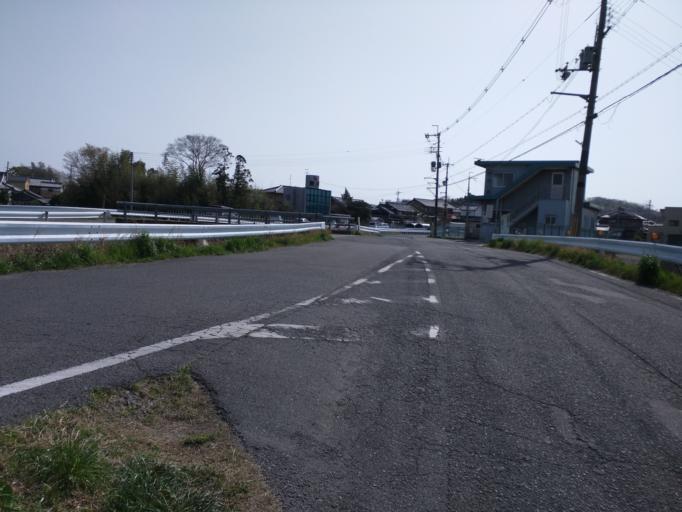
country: JP
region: Nara
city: Nara-shi
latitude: 34.7537
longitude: 135.7968
